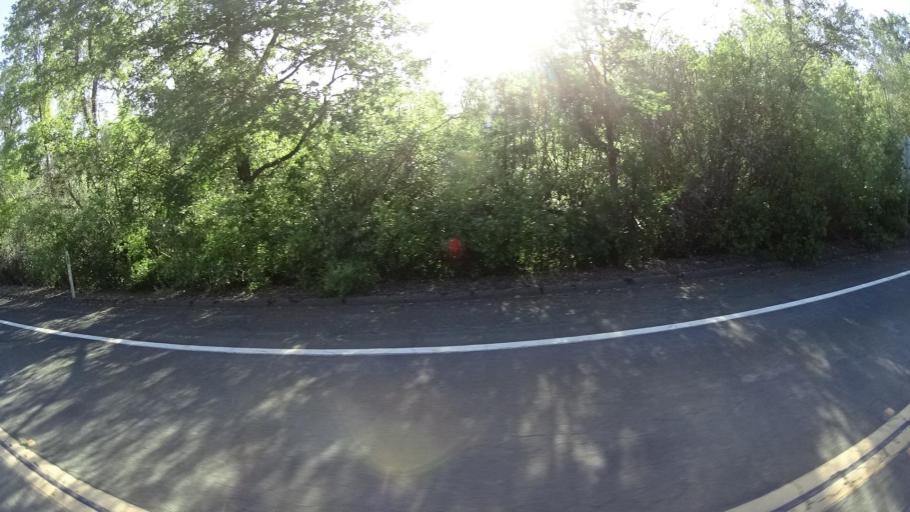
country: US
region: California
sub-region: Lake County
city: North Lakeport
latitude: 39.1095
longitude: -122.9755
